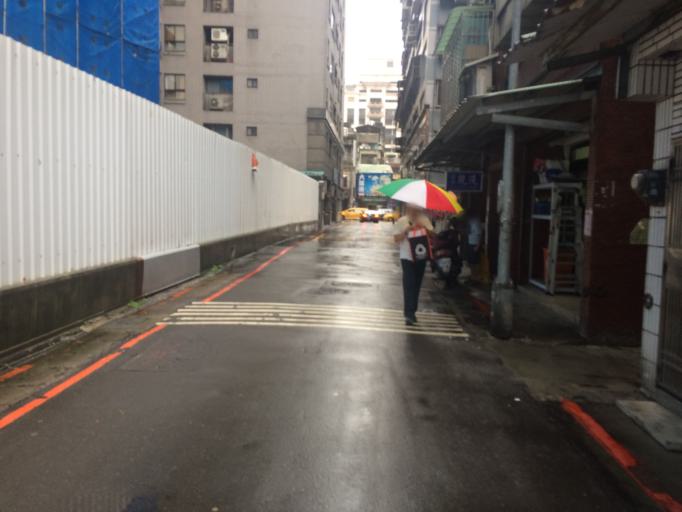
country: TW
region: Taipei
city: Taipei
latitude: 25.0399
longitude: 121.5054
